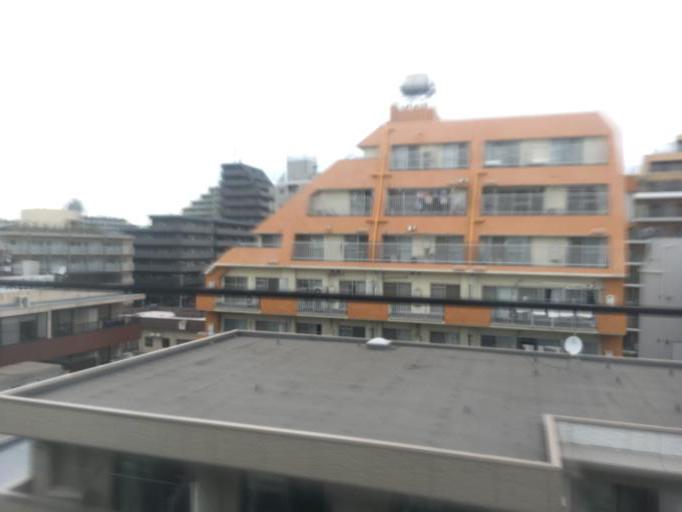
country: JP
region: Tokyo
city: Urayasu
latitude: 35.6651
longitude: 139.8547
